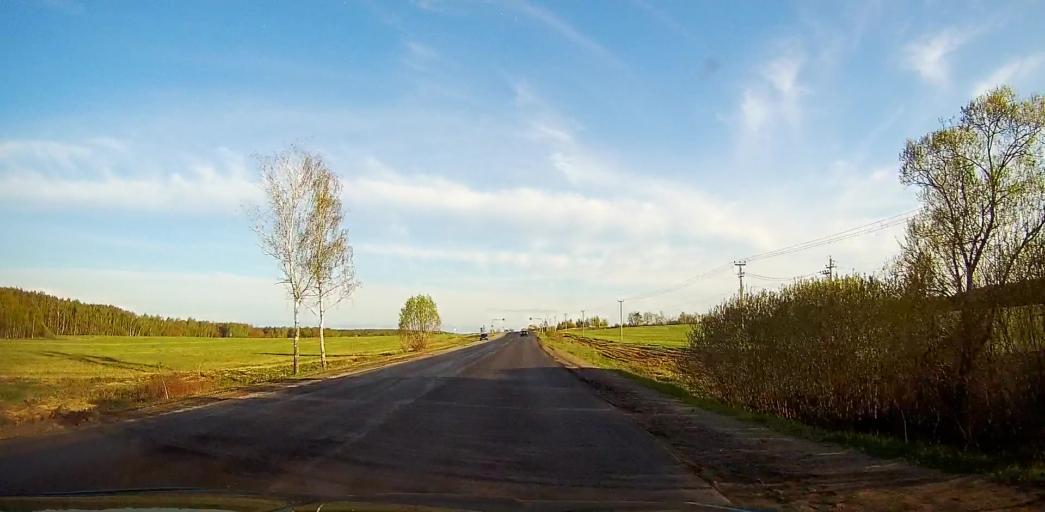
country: RU
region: Moskovskaya
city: Bronnitsy
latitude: 55.2993
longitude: 38.2109
